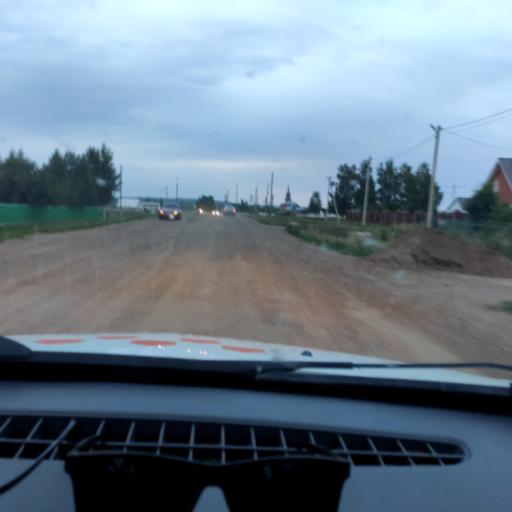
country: RU
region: Bashkortostan
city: Kabakovo
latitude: 54.5317
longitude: 56.1462
